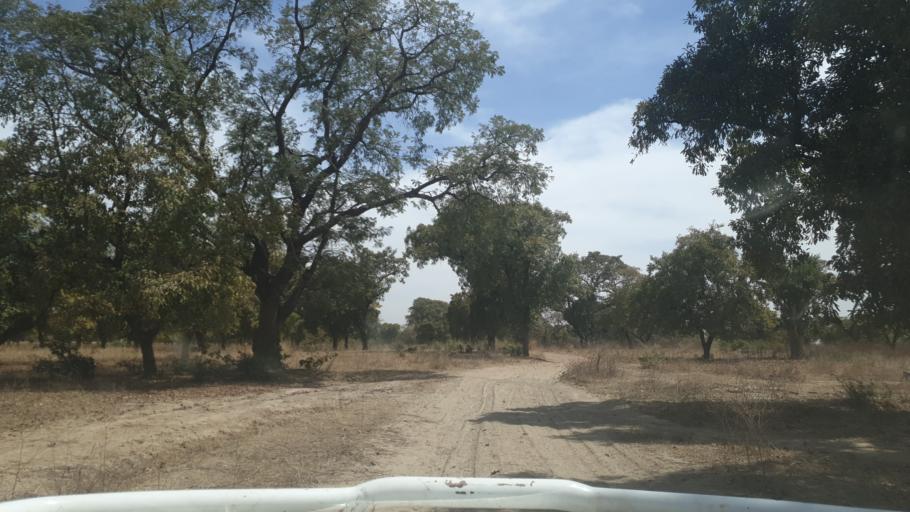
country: ML
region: Sikasso
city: Yorosso
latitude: 12.2921
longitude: -4.6640
